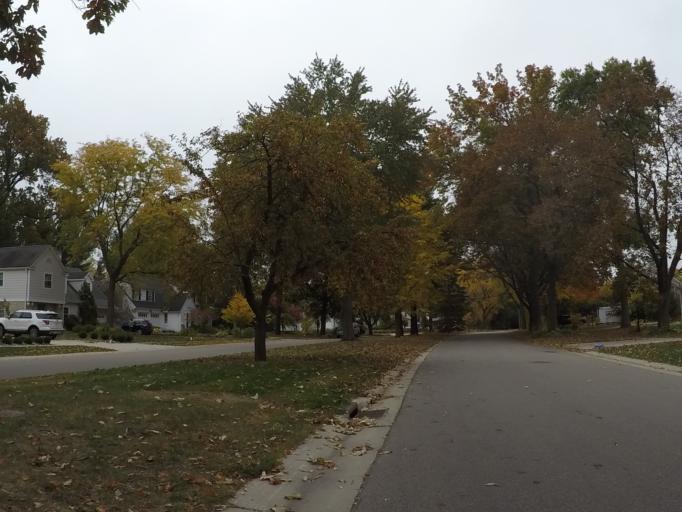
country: US
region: Wisconsin
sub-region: Dane County
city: Maple Bluff
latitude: 43.1089
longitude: -89.3670
